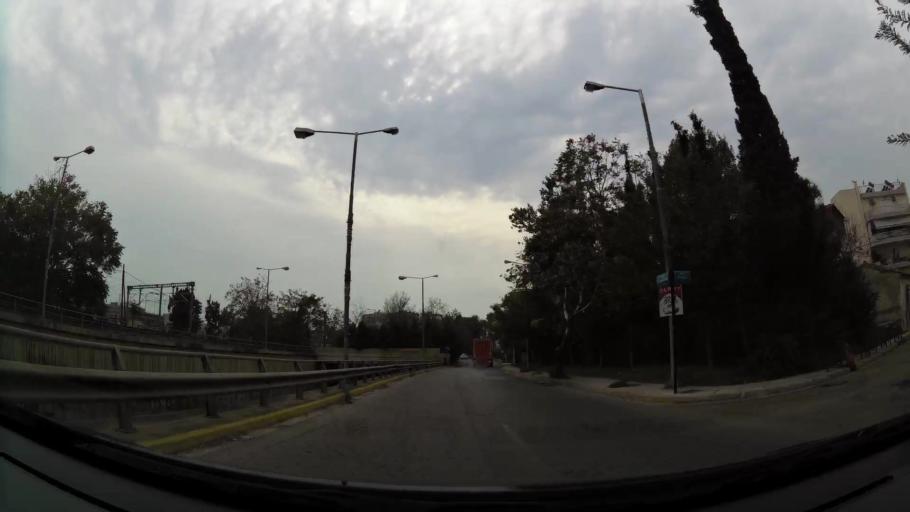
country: GR
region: Attica
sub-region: Nomarchia Athinas
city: Tavros
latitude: 37.9711
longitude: 23.6994
